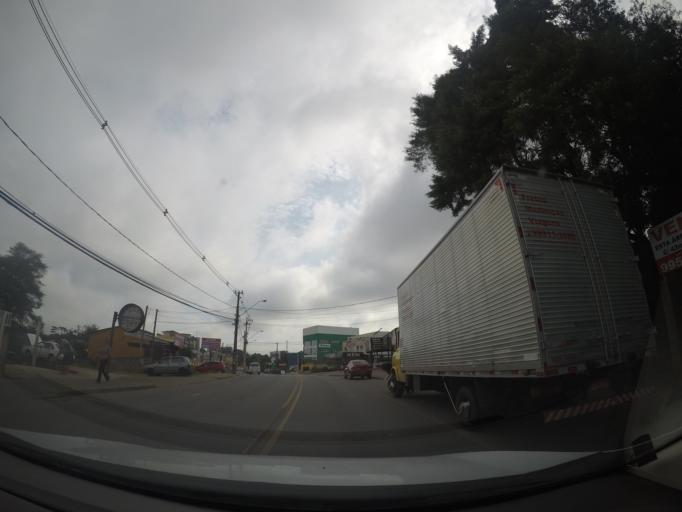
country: BR
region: Parana
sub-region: Colombo
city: Colombo
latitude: -25.3529
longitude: -49.2000
